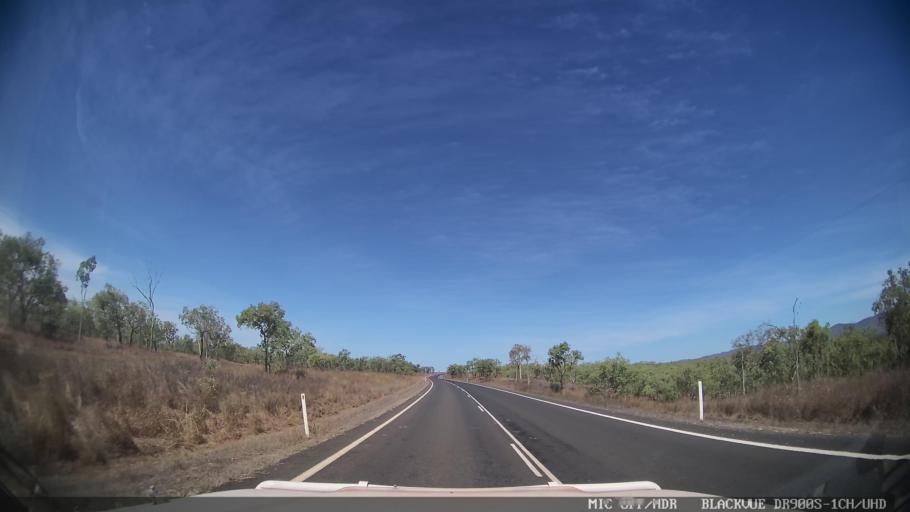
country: AU
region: Queensland
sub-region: Cook
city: Cooktown
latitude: -15.7896
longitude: 144.7048
